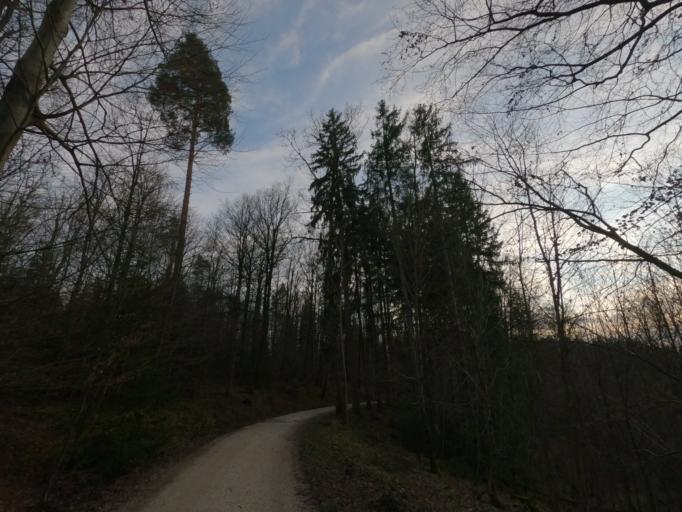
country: DE
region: Baden-Wuerttemberg
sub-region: Regierungsbezirk Stuttgart
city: Eislingen
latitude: 48.7257
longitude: 9.7091
